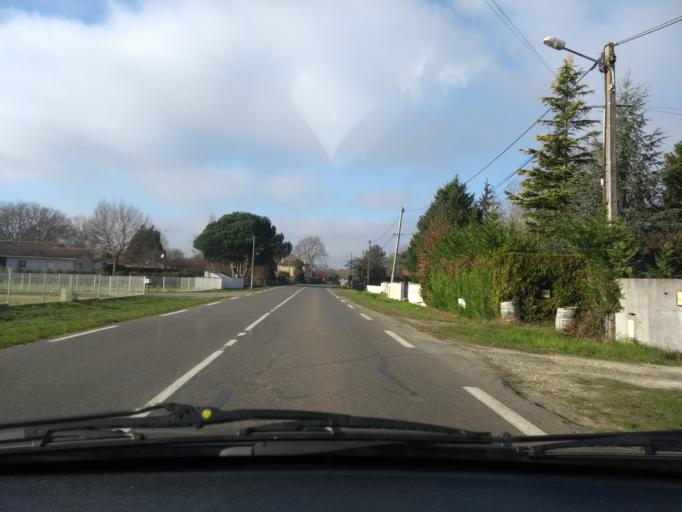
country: FR
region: Aquitaine
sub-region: Departement de la Gironde
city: Mios
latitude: 44.5943
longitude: -0.9048
